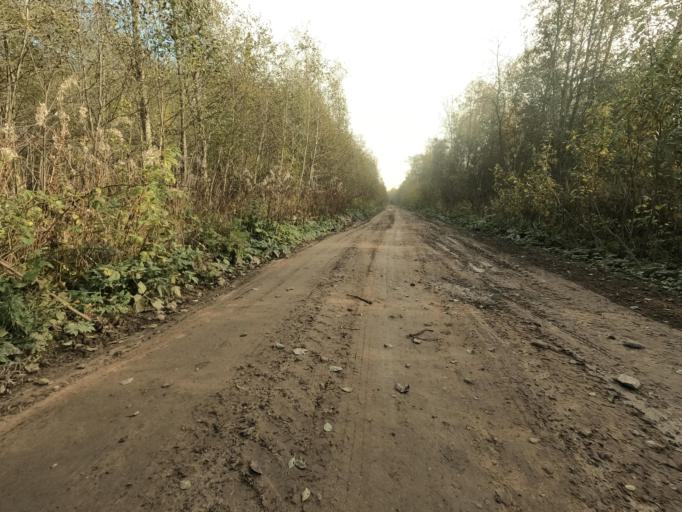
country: RU
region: Novgorod
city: Batetskiy
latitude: 58.8794
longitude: 30.7407
